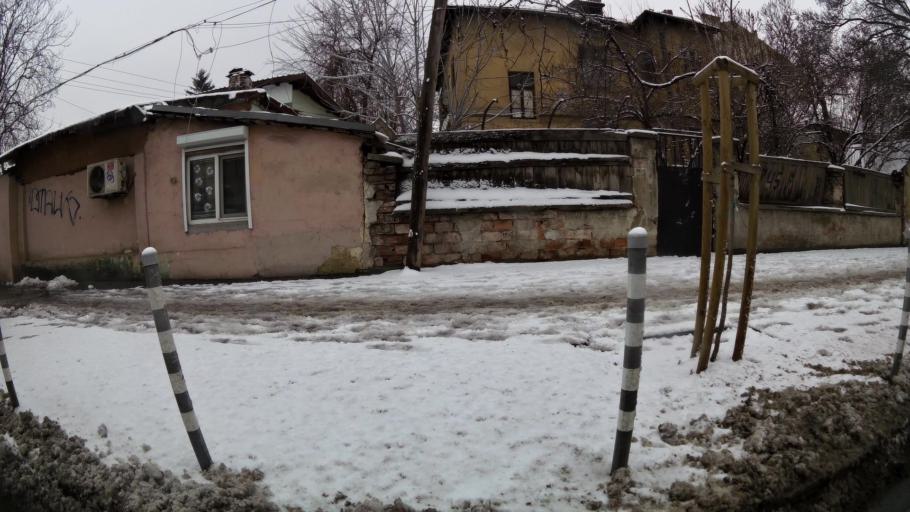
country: BG
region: Sofia-Capital
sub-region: Stolichna Obshtina
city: Sofia
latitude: 42.7057
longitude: 23.3325
